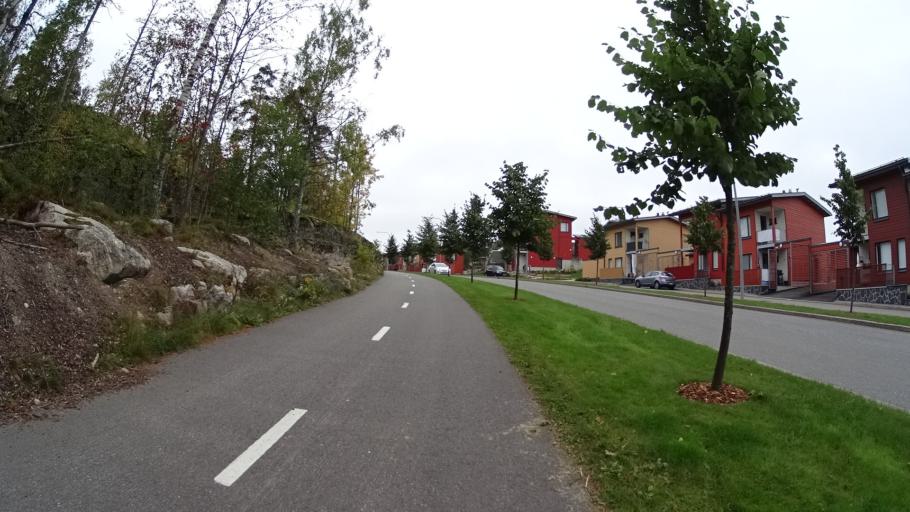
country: FI
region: Uusimaa
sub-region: Helsinki
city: Vantaa
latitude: 60.2168
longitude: 25.0608
